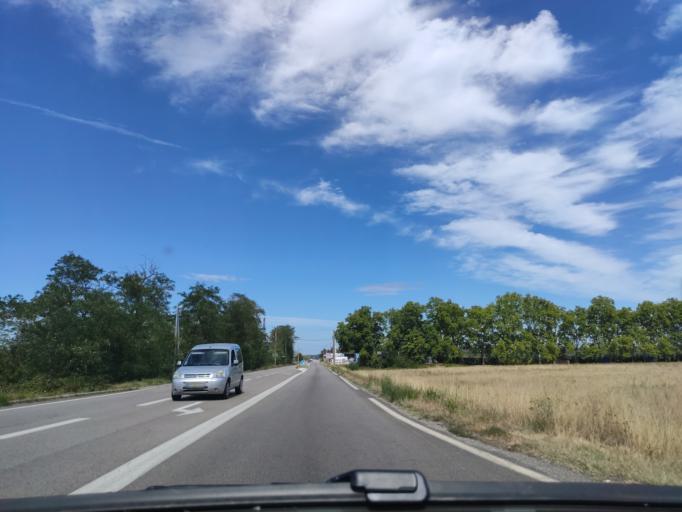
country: FR
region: Rhone-Alpes
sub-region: Departement de l'Isere
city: Clonas-sur-Vareze
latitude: 45.3998
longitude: 4.8086
